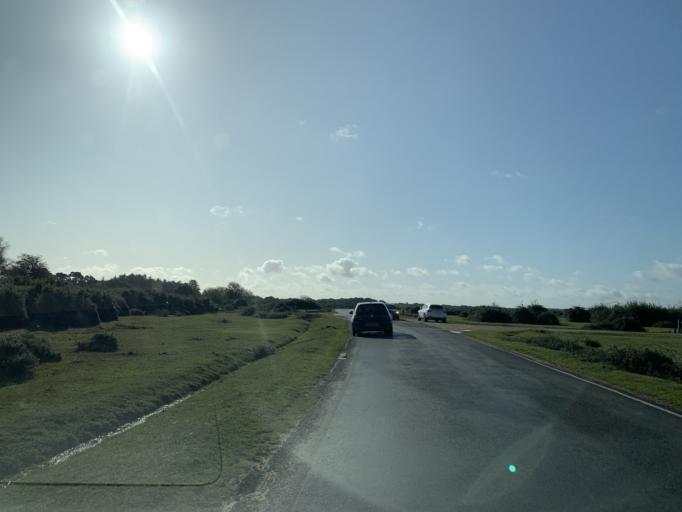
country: GB
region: England
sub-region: Hampshire
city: Cadnam
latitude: 50.9216
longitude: -1.6523
